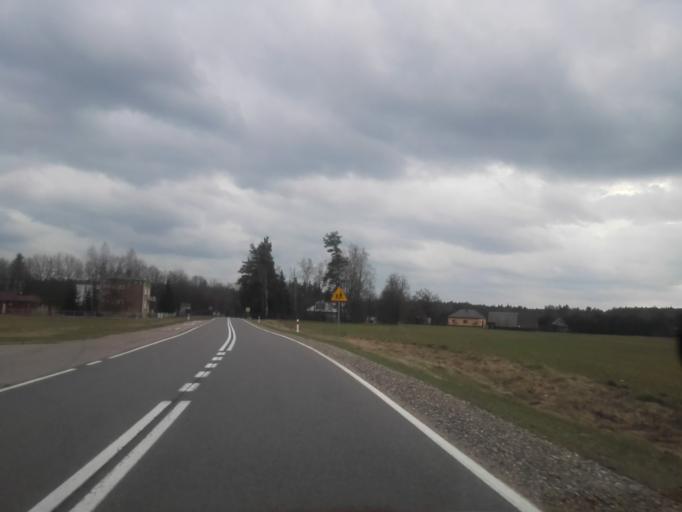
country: PL
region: Podlasie
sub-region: Powiat sejnenski
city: Sejny
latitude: 53.9824
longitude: 23.2944
